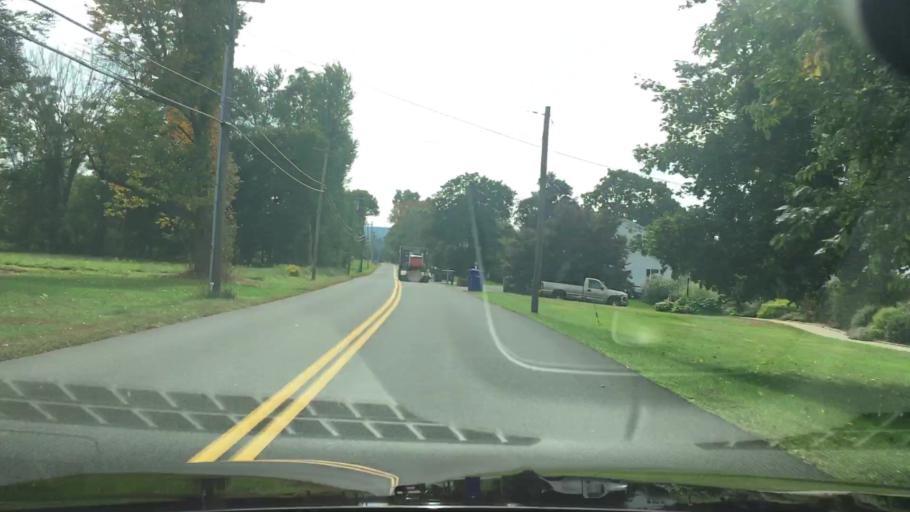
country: US
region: Connecticut
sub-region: Tolland County
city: Ellington
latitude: 41.9269
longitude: -72.4776
